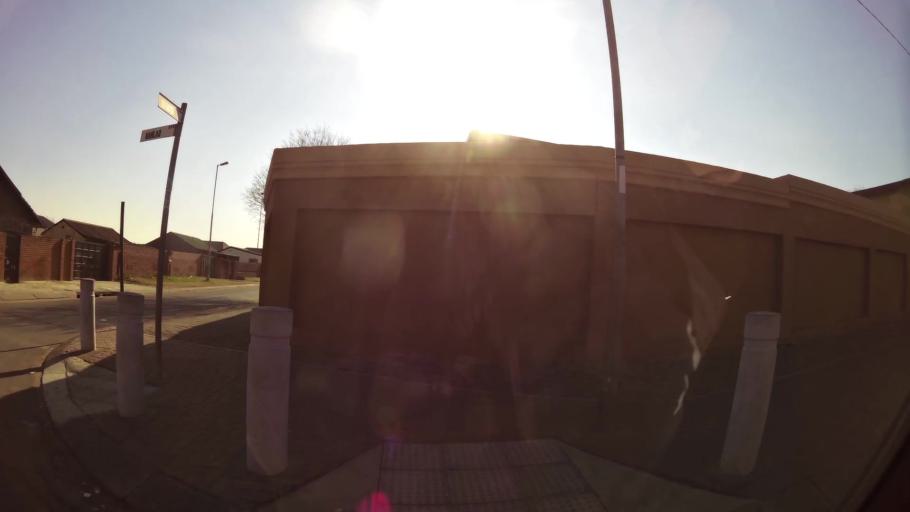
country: ZA
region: Gauteng
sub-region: City of Johannesburg Metropolitan Municipality
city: Soweto
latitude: -26.2361
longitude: 27.9250
